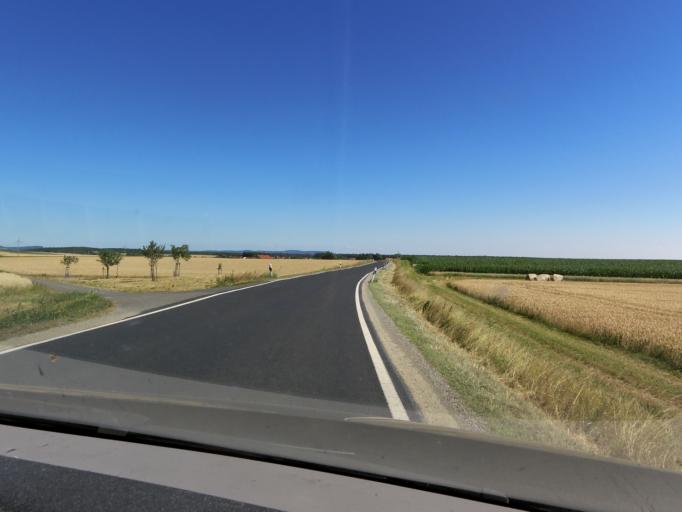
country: DE
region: Bavaria
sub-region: Regierungsbezirk Unterfranken
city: Biebelried
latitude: 49.7412
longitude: 10.0743
